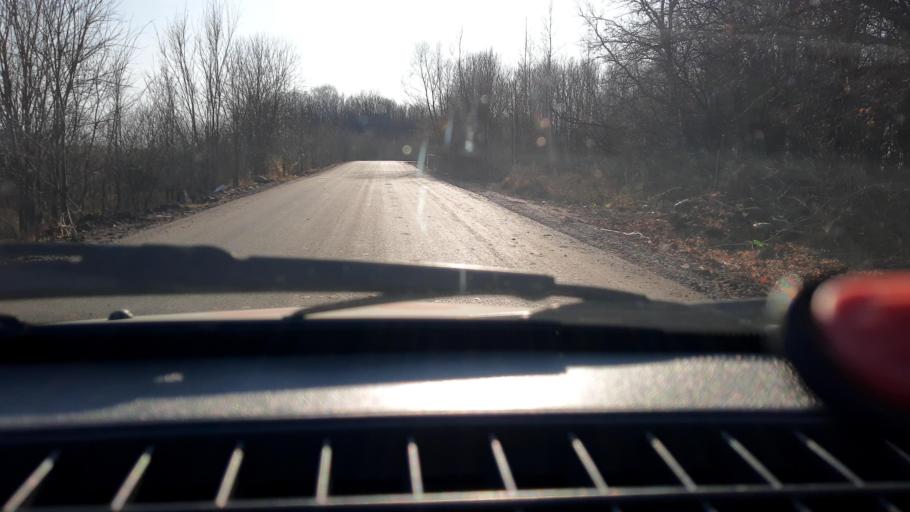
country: RU
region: Bashkortostan
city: Kabakovo
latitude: 54.6188
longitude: 56.1531
